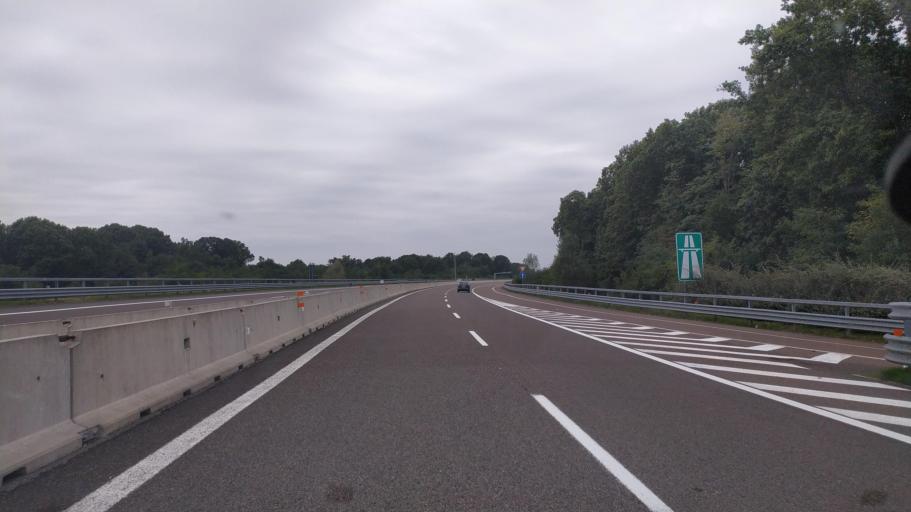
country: IT
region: Lombardy
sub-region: Provincia di Como
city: Carbonate
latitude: 45.6619
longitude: 8.9314
